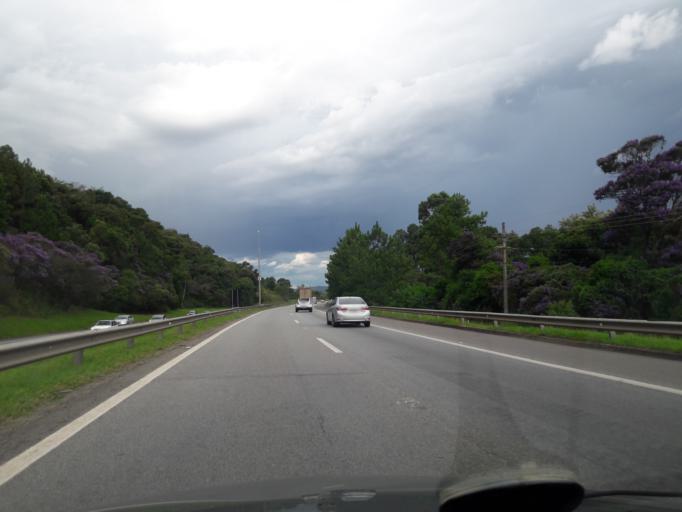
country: BR
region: Sao Paulo
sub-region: Atibaia
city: Atibaia
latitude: -23.0985
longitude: -46.5449
